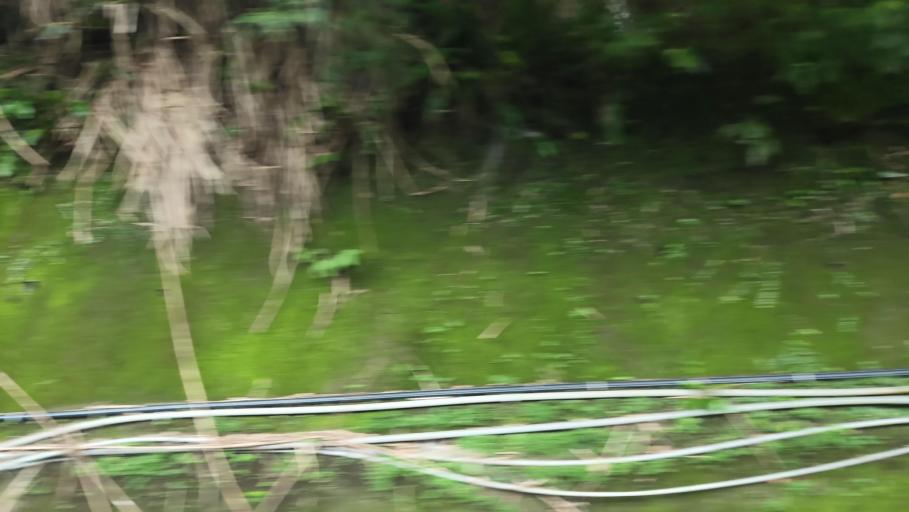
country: TW
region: Taiwan
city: Daxi
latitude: 24.8871
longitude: 121.4212
